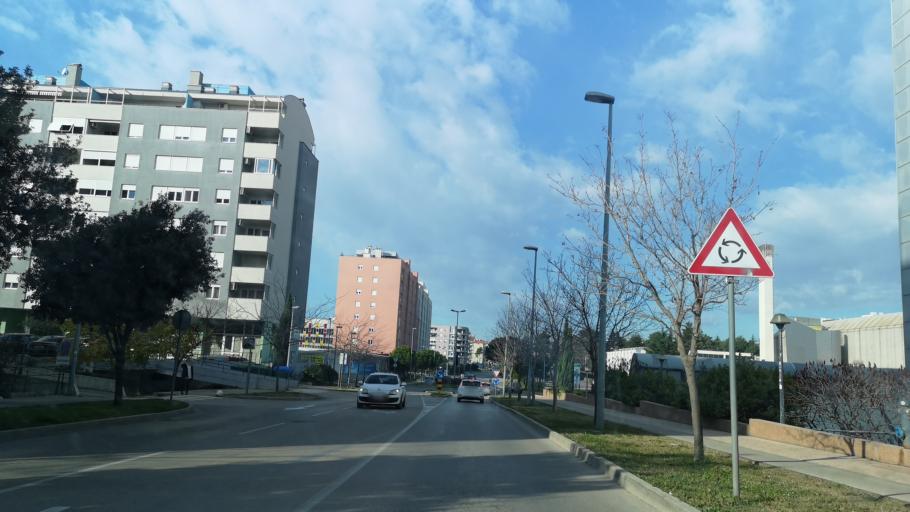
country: HR
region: Zadarska
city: Zadar
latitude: 44.1201
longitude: 15.2400
